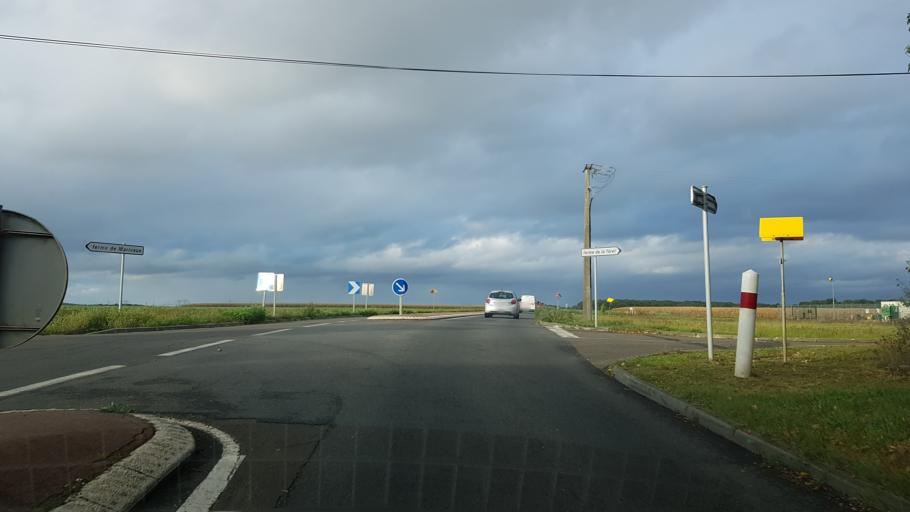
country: FR
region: Ile-de-France
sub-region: Departement de l'Essonne
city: Fontenay-les-Briis
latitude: 48.6322
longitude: 2.1769
